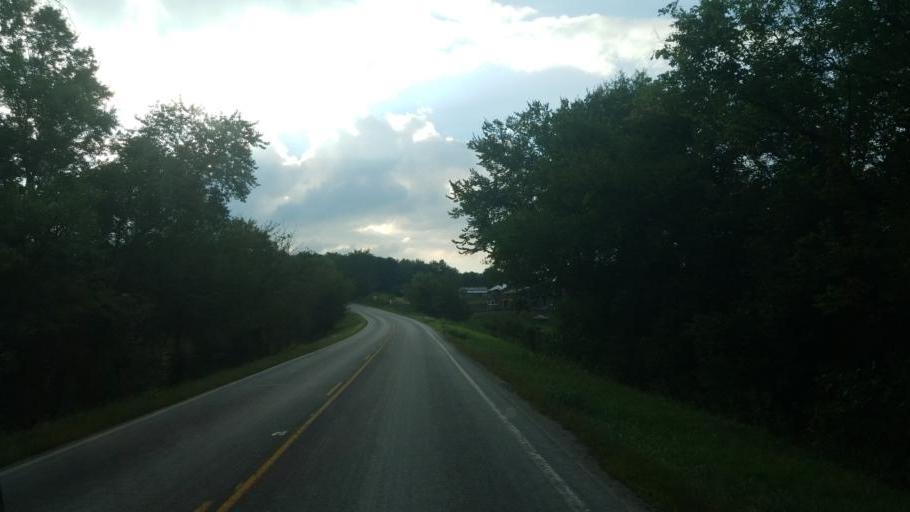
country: US
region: Ohio
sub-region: Wayne County
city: Shreve
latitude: 40.7496
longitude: -82.1362
